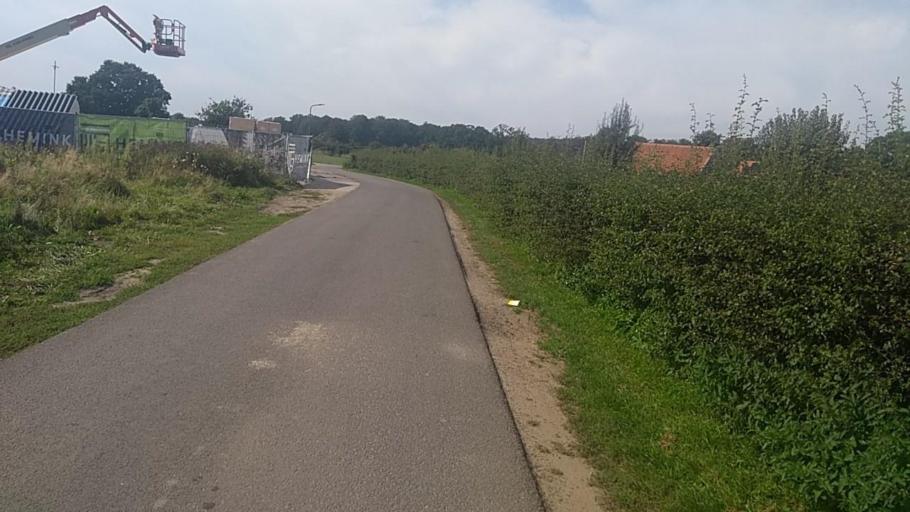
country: NL
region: Gelderland
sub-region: Gemeente Rheden
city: Rheden
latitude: 52.0019
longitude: 6.0216
